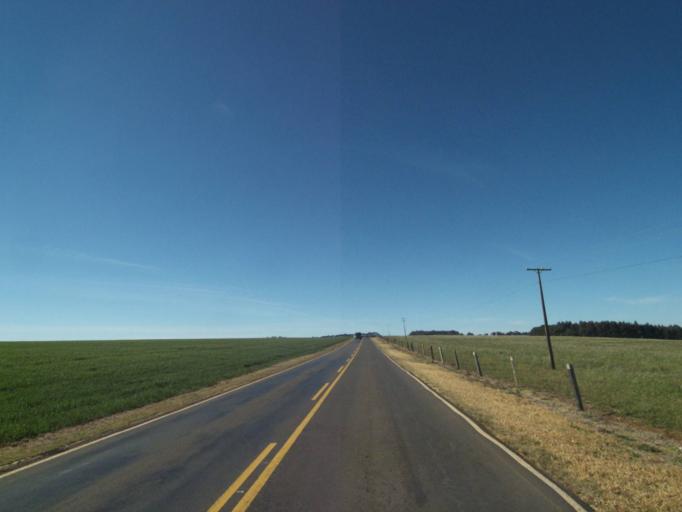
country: BR
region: Parana
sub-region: Tibagi
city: Tibagi
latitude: -24.5435
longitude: -50.3029
